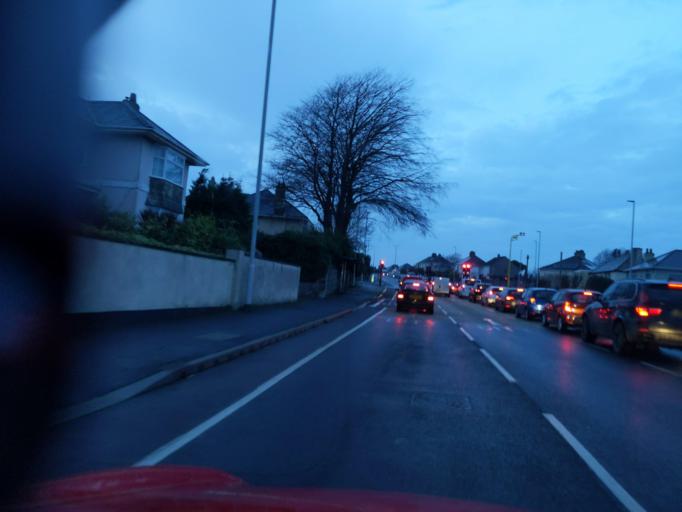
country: GB
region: England
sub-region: Plymouth
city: Plymstock
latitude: 50.3608
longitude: -4.0650
